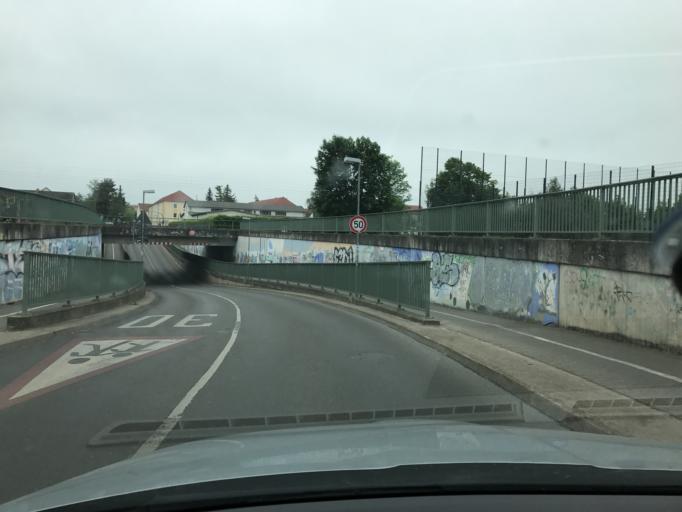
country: DE
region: Brandenburg
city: Falkensee
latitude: 52.5634
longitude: 13.0781
